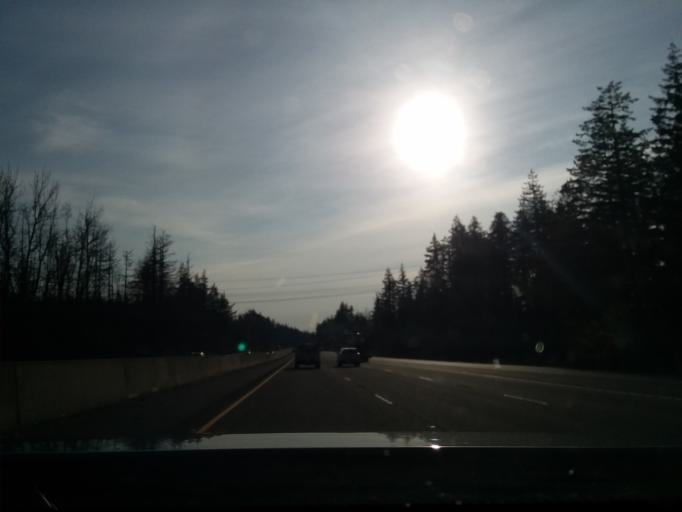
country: US
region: Washington
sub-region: Thurston County
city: Grand Mound
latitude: 46.8691
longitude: -122.9698
